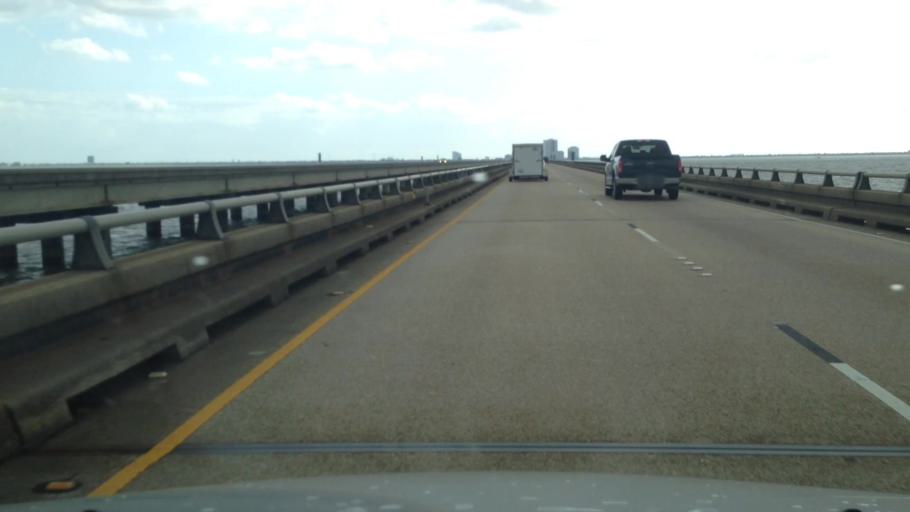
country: US
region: Louisiana
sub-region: Jefferson Parish
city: Metairie
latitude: 30.0677
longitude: -90.1460
